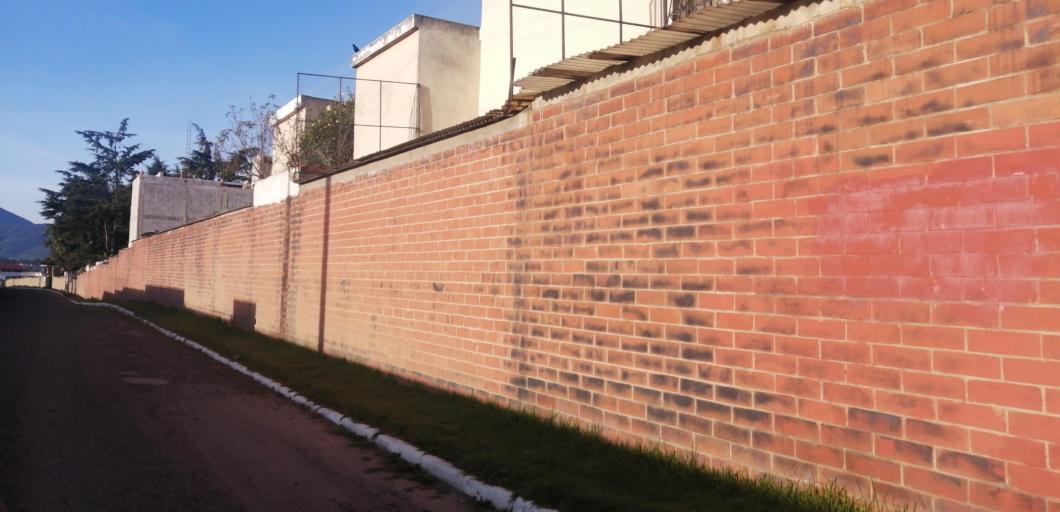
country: GT
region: Quetzaltenango
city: Olintepeque
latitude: 14.8676
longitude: -91.5329
